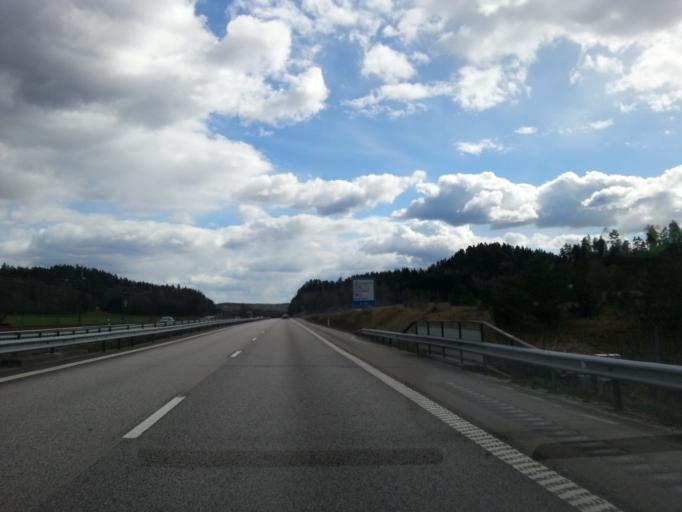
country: SE
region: Vaestra Goetaland
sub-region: Uddevalla Kommun
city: Ljungskile
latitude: 58.2521
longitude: 11.9037
